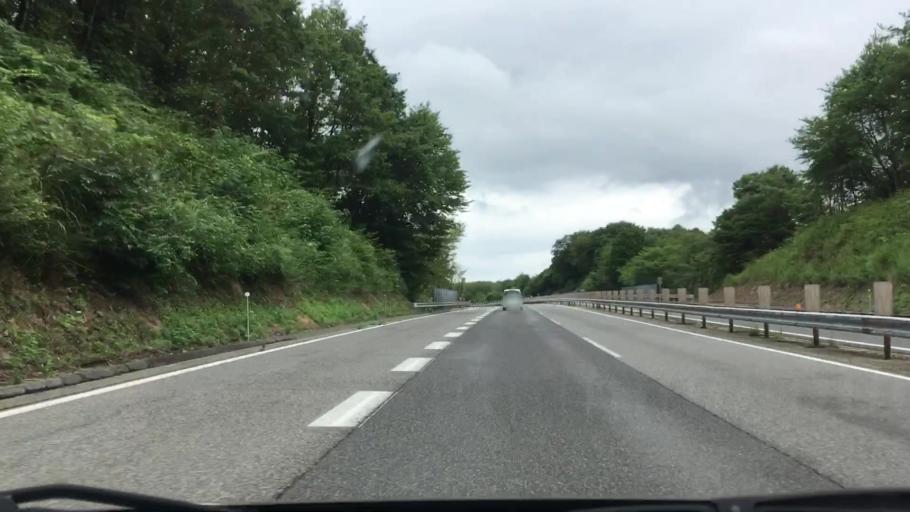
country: JP
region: Hiroshima
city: Miyoshi
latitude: 34.7545
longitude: 132.7601
